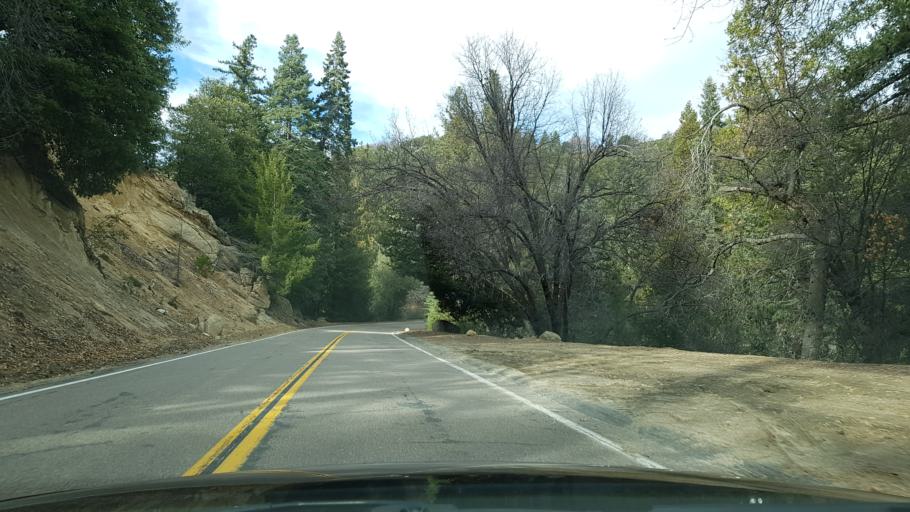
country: US
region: California
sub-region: Riverside County
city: Aguanga
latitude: 33.3432
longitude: -116.8800
